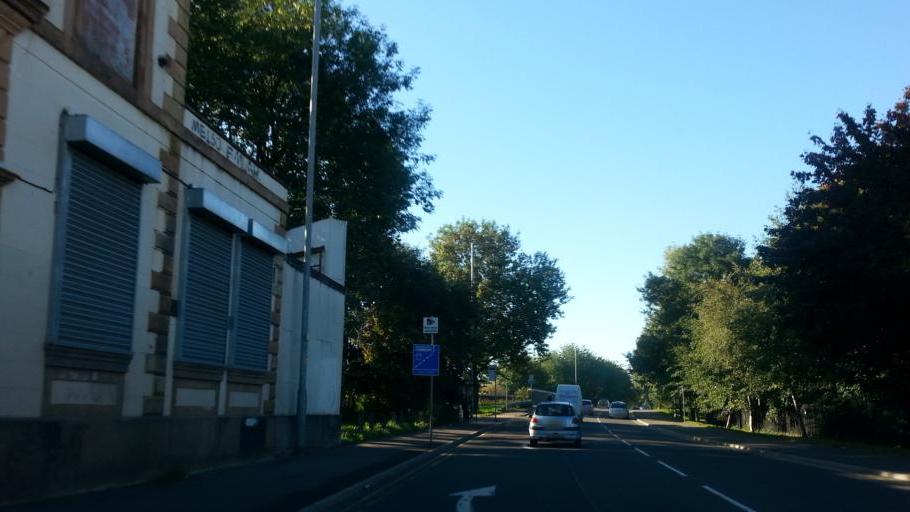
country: GB
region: England
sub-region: Manchester
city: Cheetham Hill
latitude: 53.4933
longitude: -2.2250
